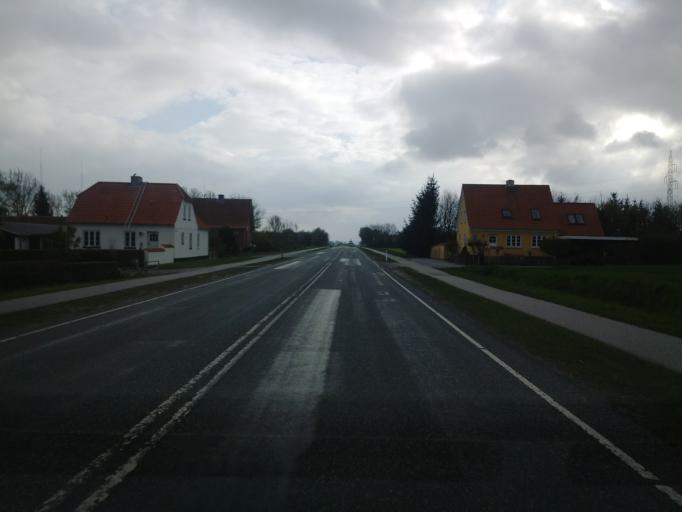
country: DK
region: North Denmark
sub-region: Frederikshavn Kommune
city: Saeby
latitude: 57.2887
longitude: 10.3814
